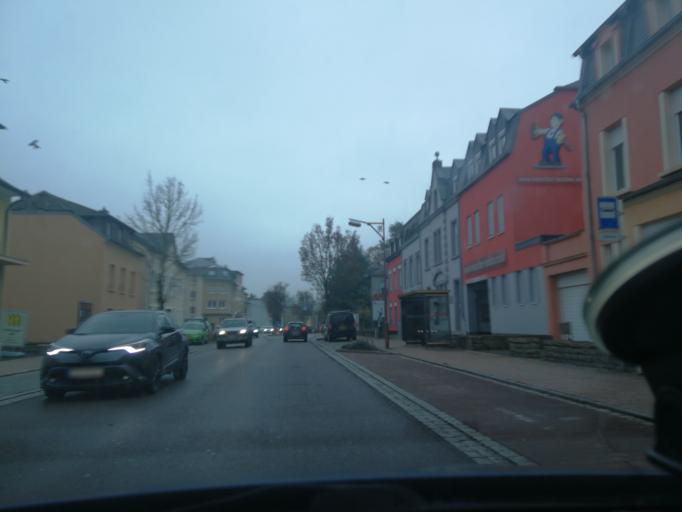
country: LU
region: Grevenmacher
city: Wasserbillig
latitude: 49.7114
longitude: 6.4942
